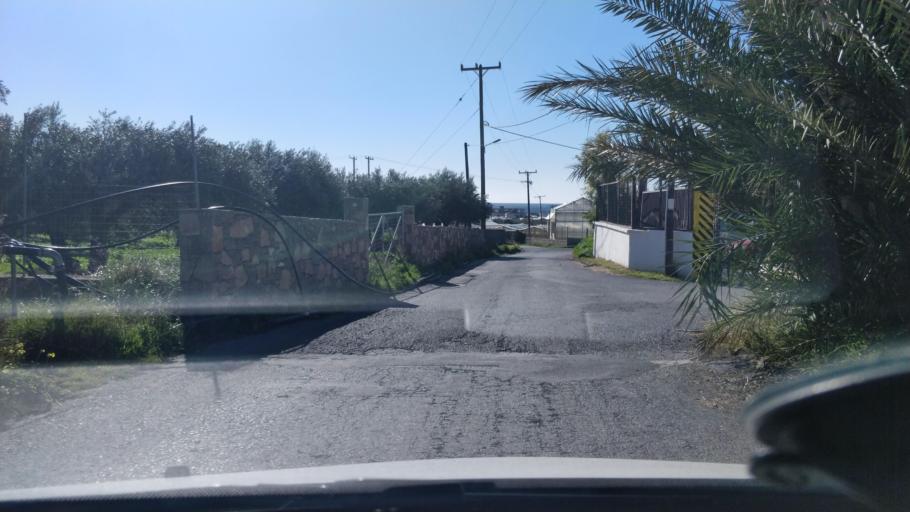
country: GR
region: Crete
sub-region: Nomos Lasithiou
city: Gra Liyia
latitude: 35.0195
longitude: 25.6784
